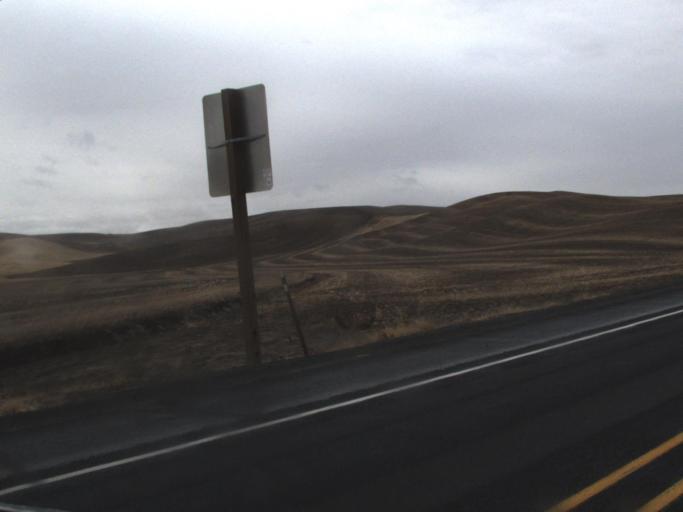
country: US
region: Washington
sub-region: Whitman County
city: Pullman
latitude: 46.5682
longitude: -117.1346
